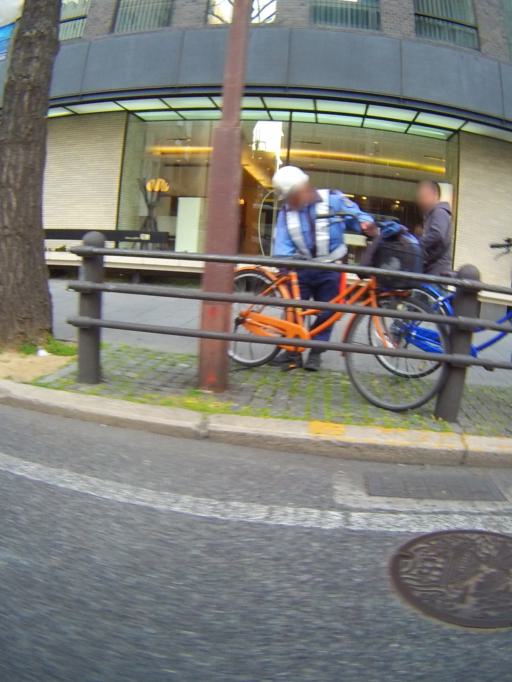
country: JP
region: Osaka
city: Osaka-shi
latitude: 34.6826
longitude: 135.5007
